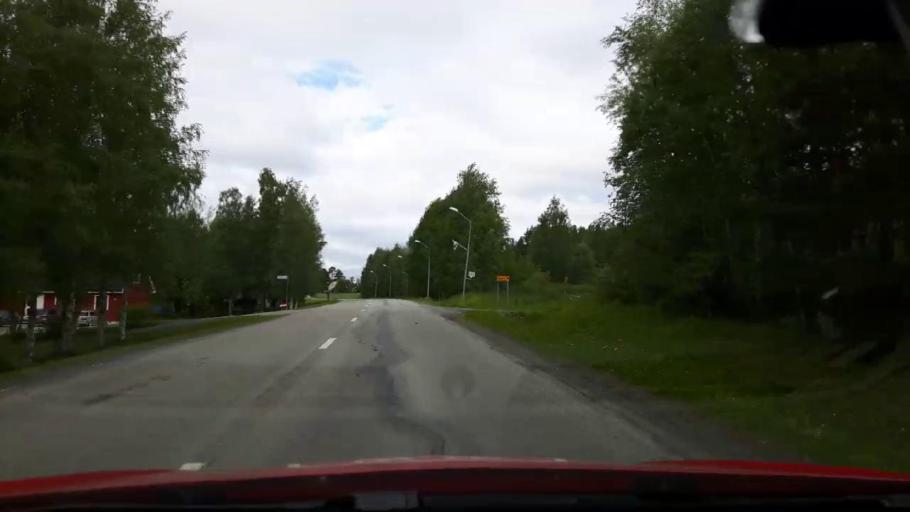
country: SE
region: Jaemtland
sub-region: Krokoms Kommun
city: Krokom
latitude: 63.2986
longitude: 14.4812
